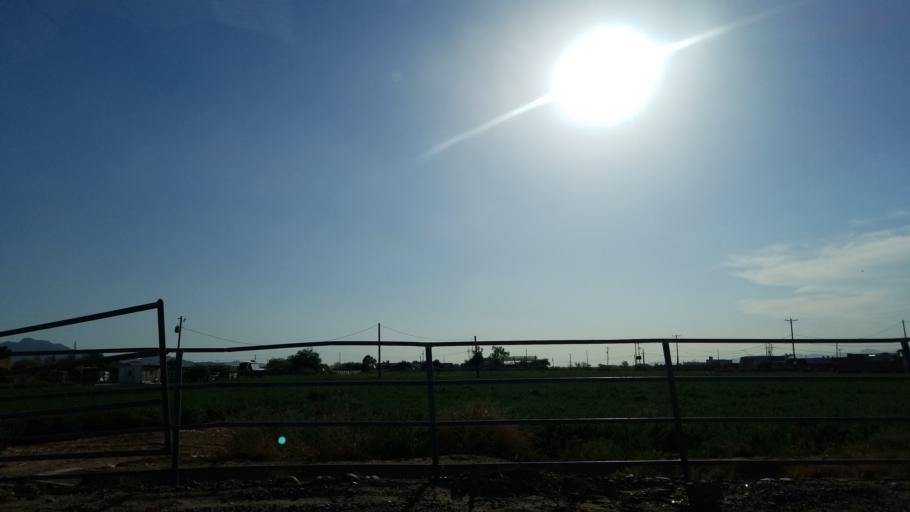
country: US
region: Arizona
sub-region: Maricopa County
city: Laveen
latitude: 33.3877
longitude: -112.2199
